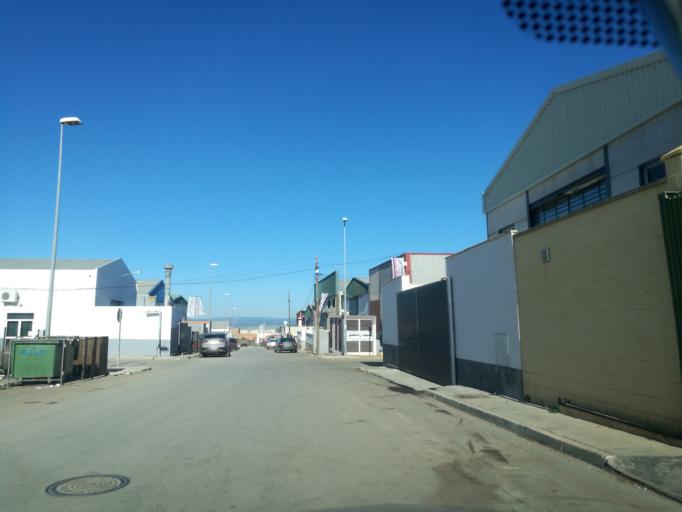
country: ES
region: Andalusia
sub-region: Provincia de Sevilla
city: La Campana
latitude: 37.5758
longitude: -5.4311
